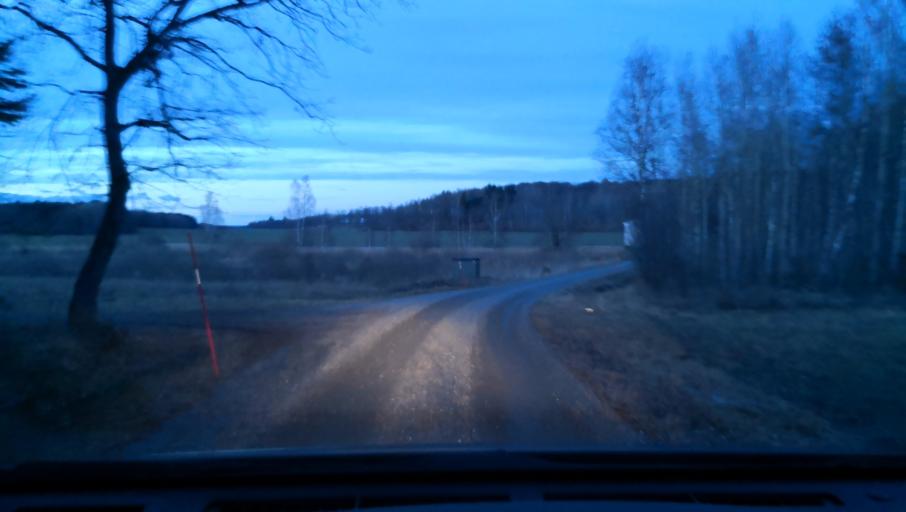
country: SE
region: Uppsala
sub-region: Enkopings Kommun
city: Dalby
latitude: 59.5661
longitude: 17.3741
